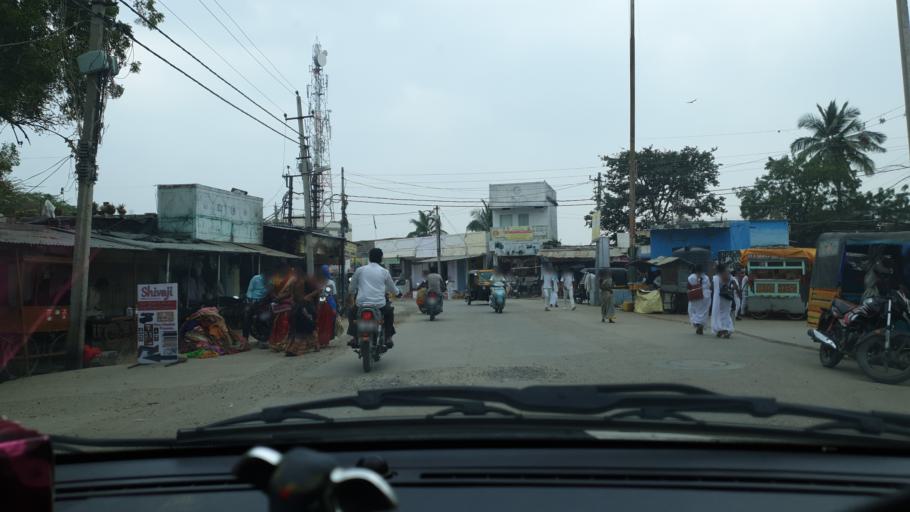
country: IN
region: Karnataka
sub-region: Yadgir
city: Gurmatkal
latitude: 16.8673
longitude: 77.3922
